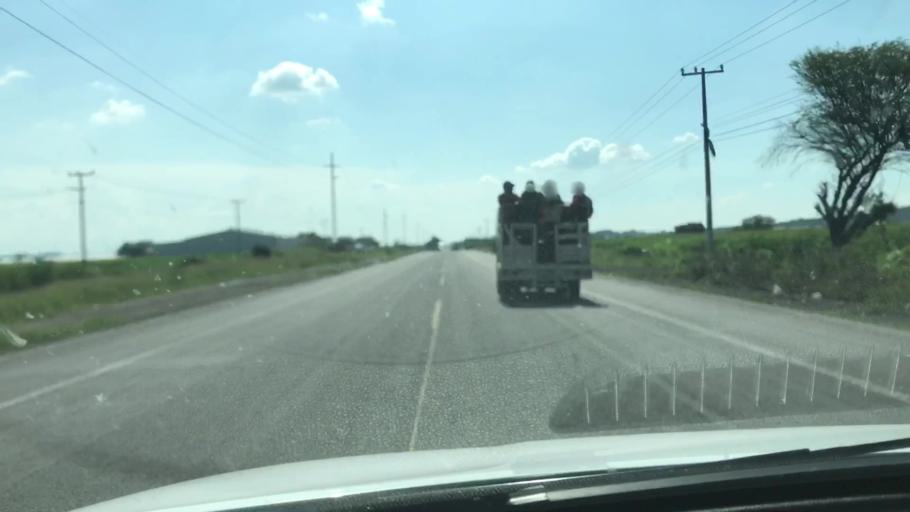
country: MX
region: Michoacan
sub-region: Vista Hermosa
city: Los Pilares
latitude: 20.2760
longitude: -102.3866
